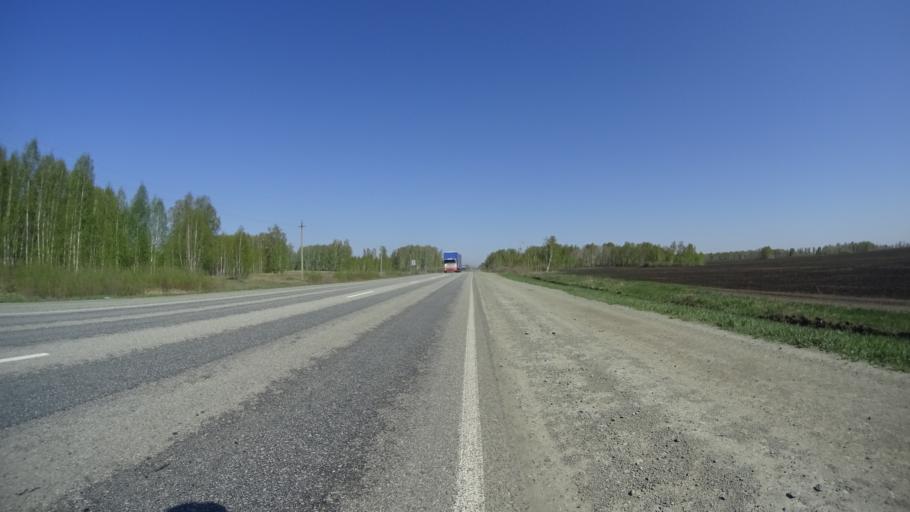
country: RU
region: Chelyabinsk
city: Troitsk
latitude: 54.1810
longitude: 61.4348
